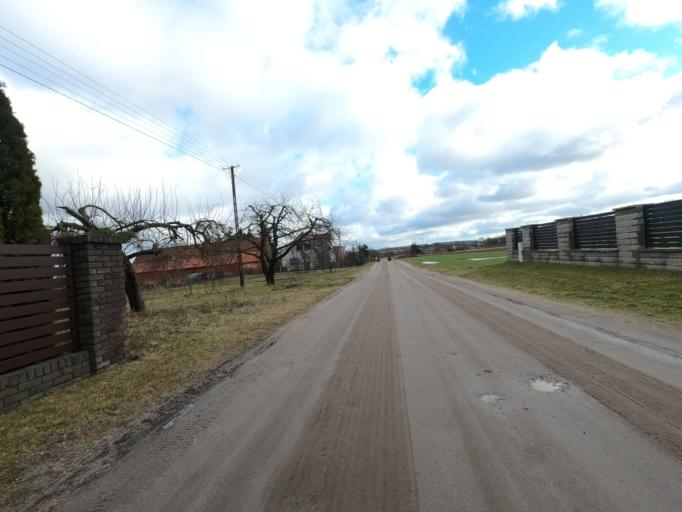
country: PL
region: Greater Poland Voivodeship
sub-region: Powiat pilski
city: Miasteczko Krajenskie
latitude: 53.1143
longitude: 16.9921
